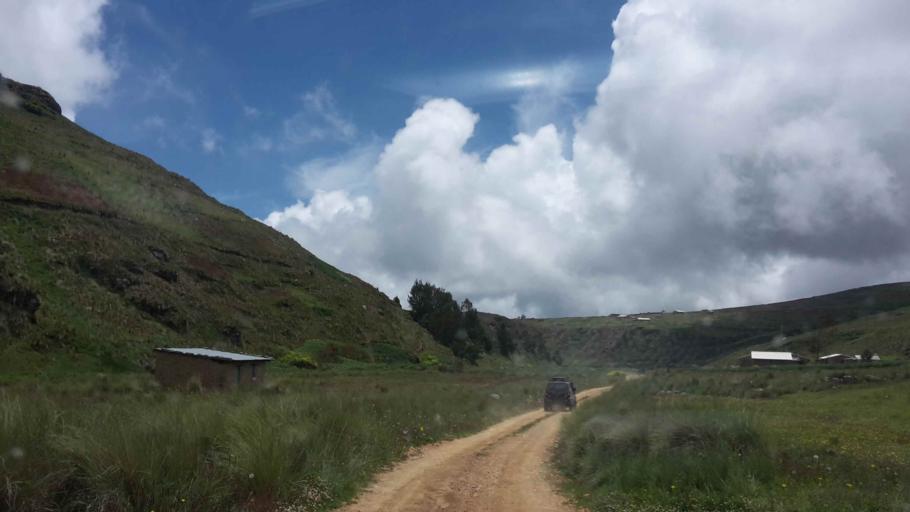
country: BO
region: Cochabamba
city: Cochabamba
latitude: -17.1851
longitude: -66.0677
